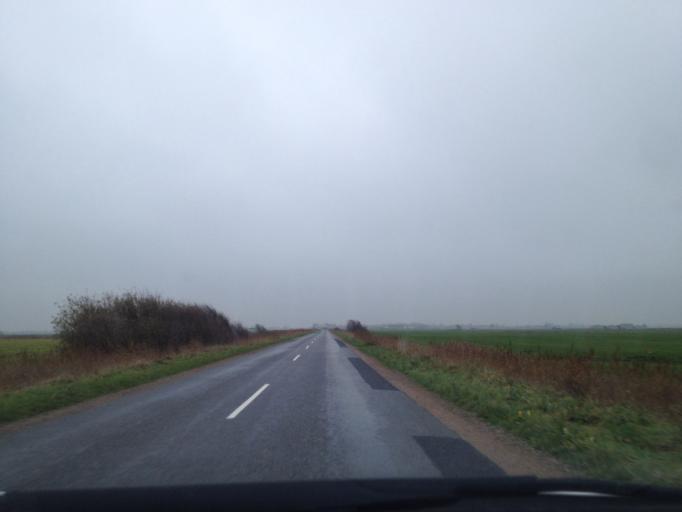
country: DK
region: South Denmark
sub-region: Tonder Kommune
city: Sherrebek
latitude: 55.1067
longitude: 8.7271
